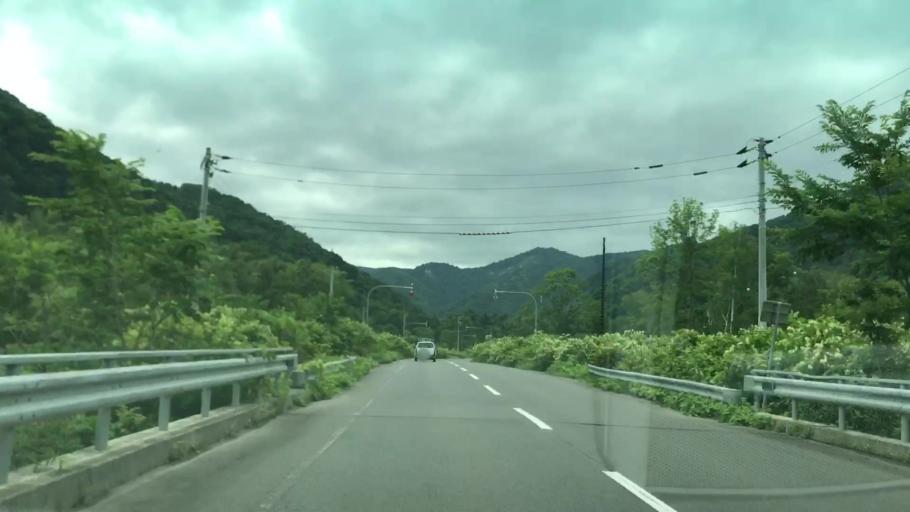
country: JP
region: Hokkaido
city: Yoichi
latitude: 43.0275
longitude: 140.8663
